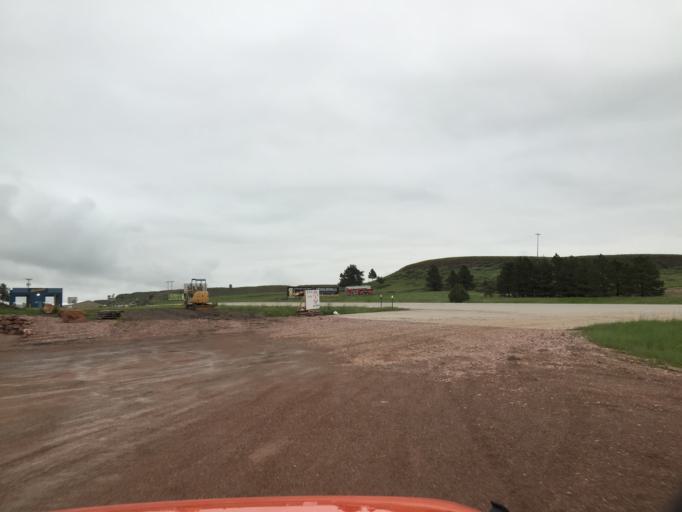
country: US
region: South Dakota
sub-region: Fall River County
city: Hot Springs
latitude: 43.4010
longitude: -103.3966
